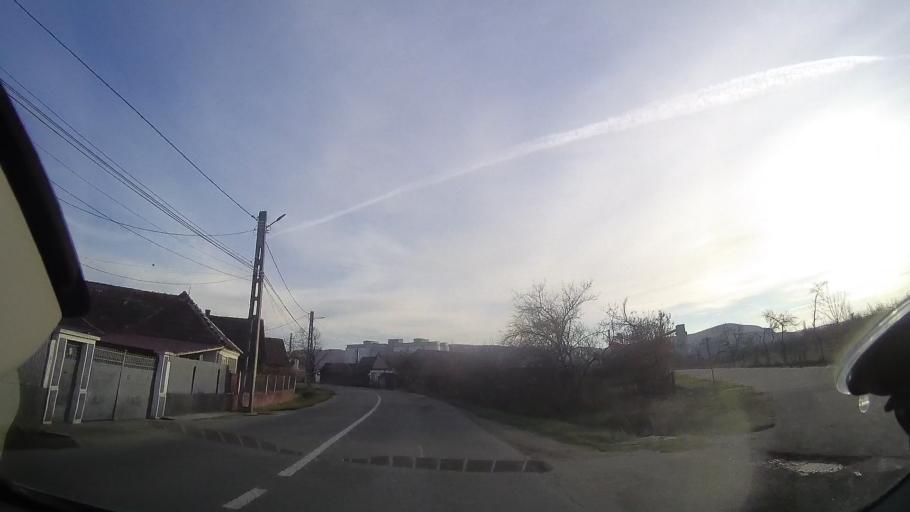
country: RO
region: Bihor
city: Lugasu de Jos
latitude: 47.0454
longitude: 22.3317
